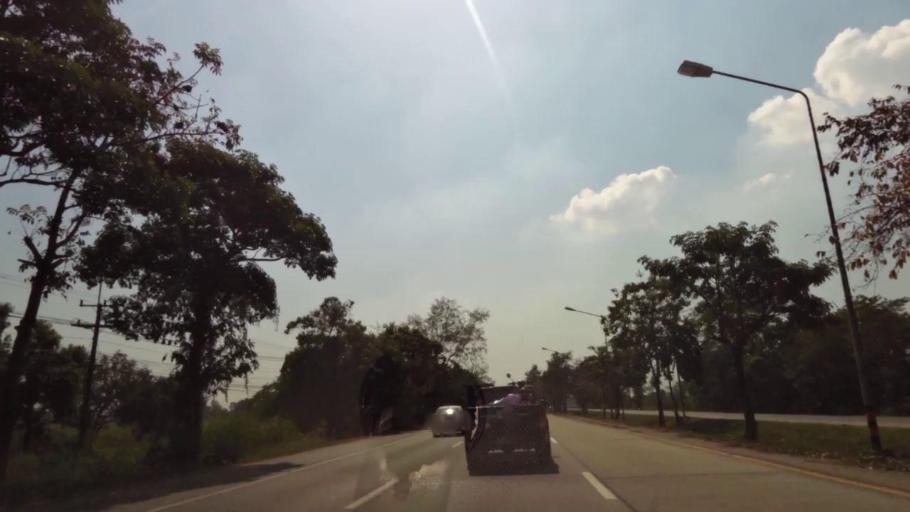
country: TH
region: Phichit
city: Wachira Barami
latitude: 16.5471
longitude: 100.1460
